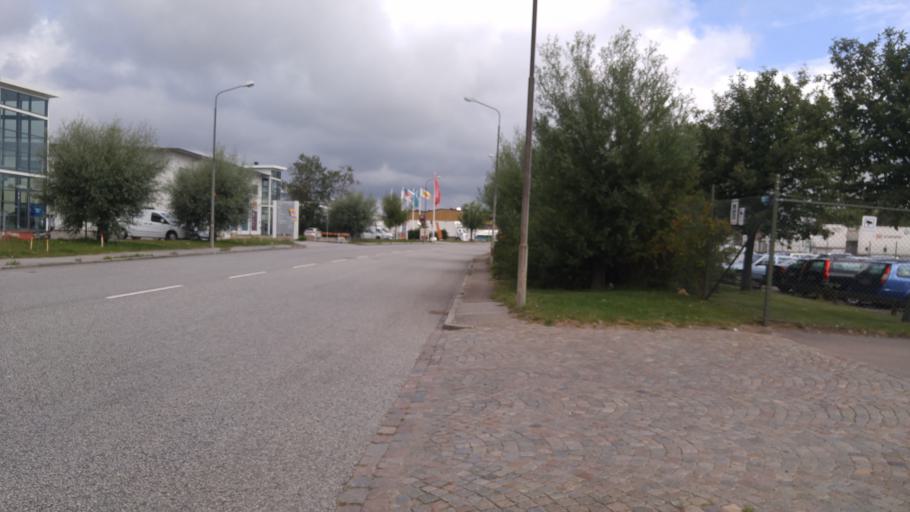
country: SE
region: Skane
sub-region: Malmo
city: Oxie
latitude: 55.5562
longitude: 13.0464
